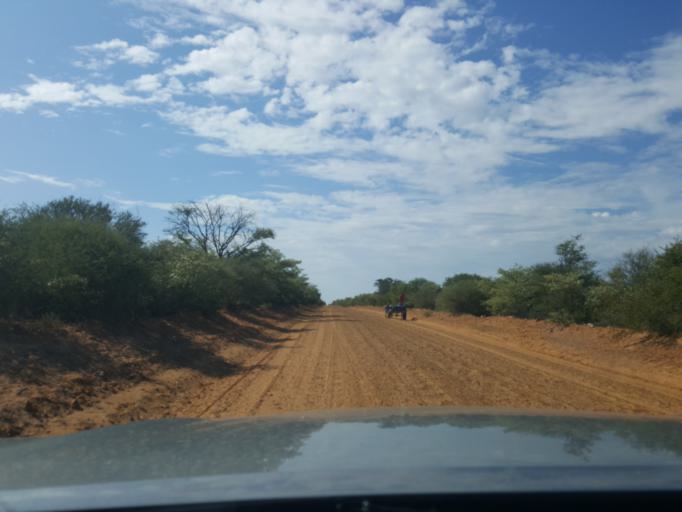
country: BW
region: Kweneng
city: Khudumelapye
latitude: -23.6370
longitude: 24.7296
